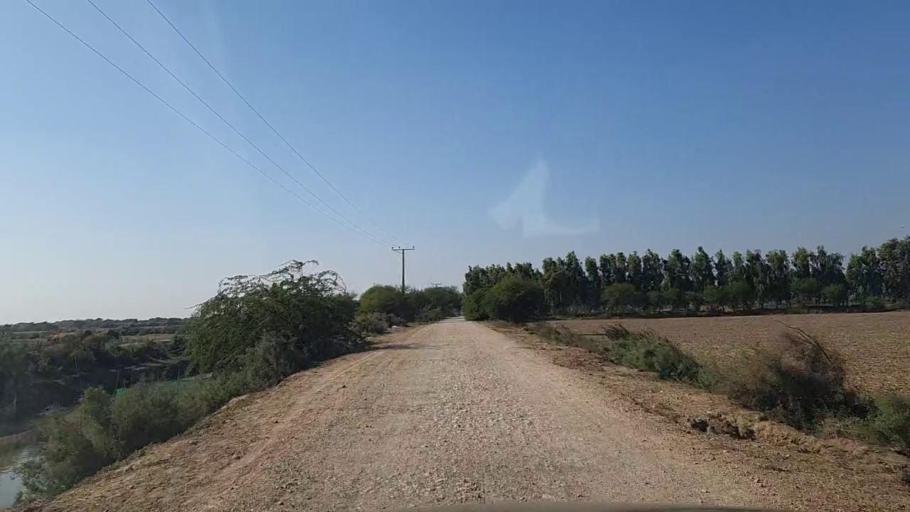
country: PK
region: Sindh
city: Mirpur Batoro
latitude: 24.7357
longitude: 68.3442
